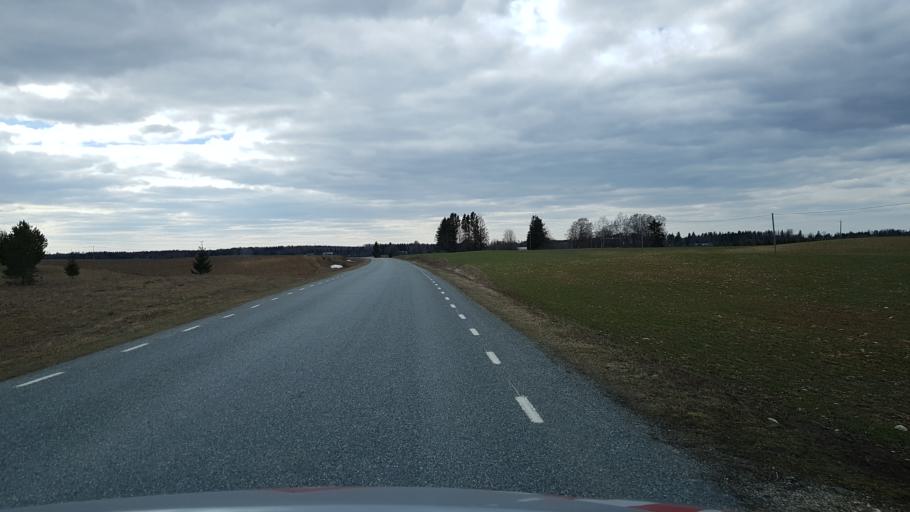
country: EE
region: Laeaene-Virumaa
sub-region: Rakvere linn
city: Rakvere
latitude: 59.2650
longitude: 26.2614
